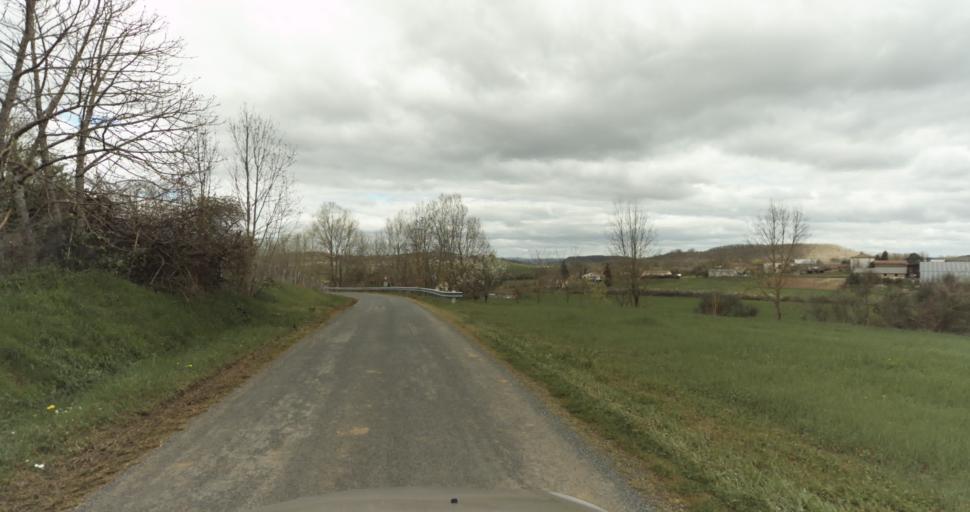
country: FR
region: Midi-Pyrenees
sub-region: Departement du Tarn
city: Puygouzon
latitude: 43.8729
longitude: 2.1795
